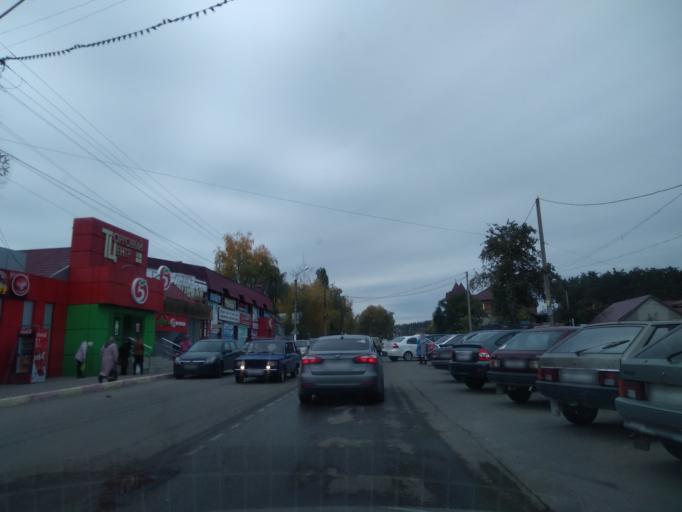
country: RU
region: Lipetsk
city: Zadonsk
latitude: 52.3885
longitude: 38.9350
